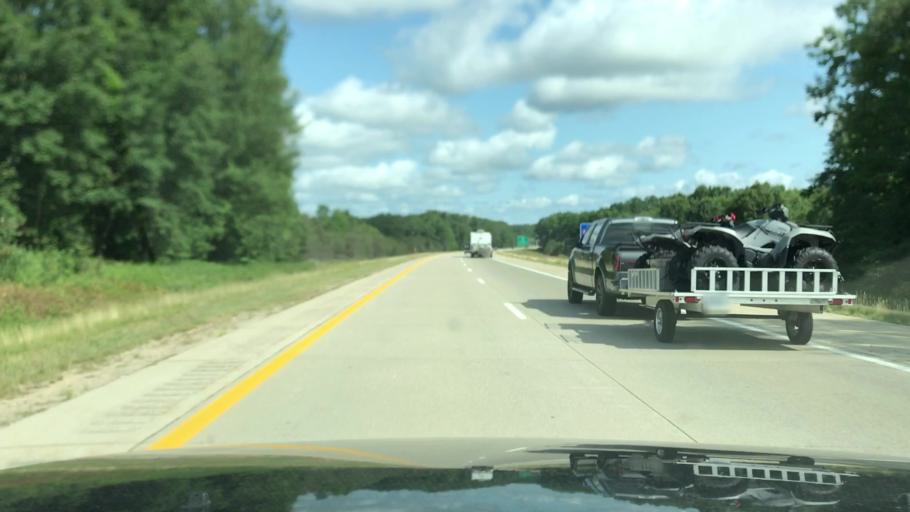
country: US
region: Michigan
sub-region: Montcalm County
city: Howard City
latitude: 43.3729
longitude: -85.5169
